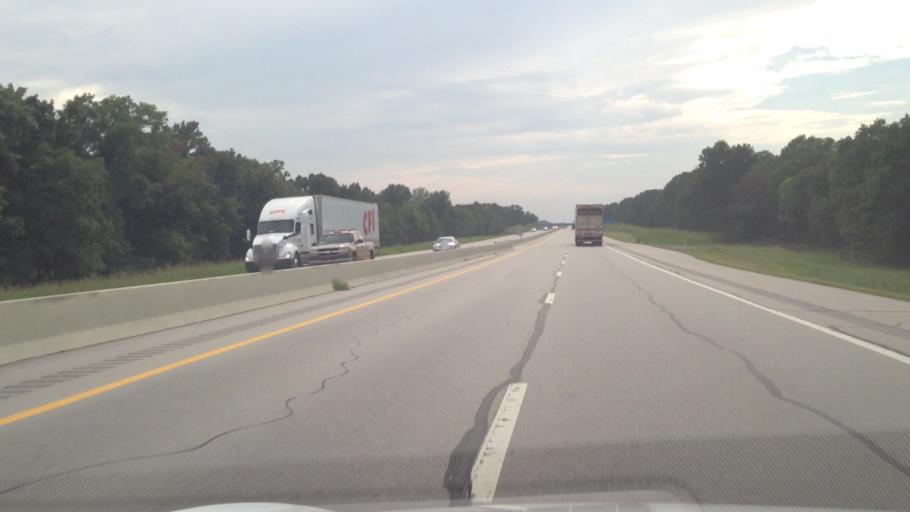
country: US
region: Kansas
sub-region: Cherokee County
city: Baxter Springs
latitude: 36.9323
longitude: -94.7193
